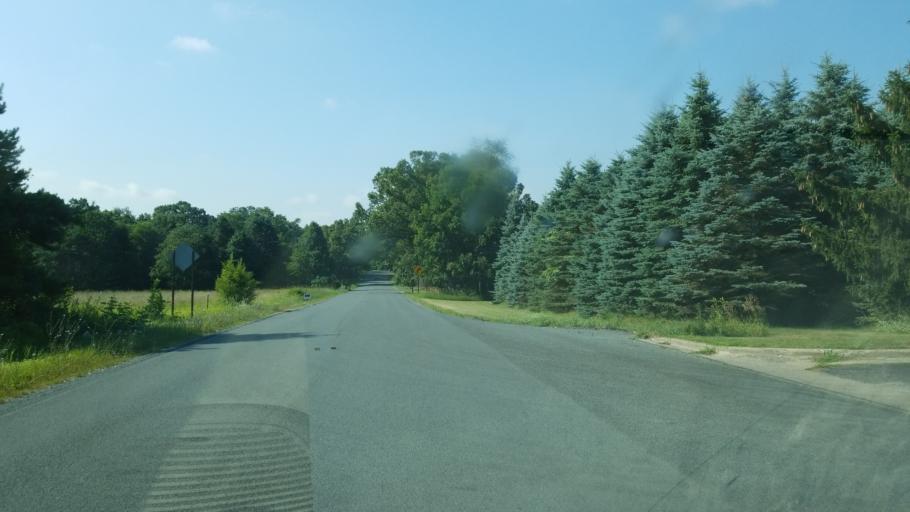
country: US
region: Michigan
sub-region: Kent County
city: Sparta
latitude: 43.1368
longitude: -85.6409
